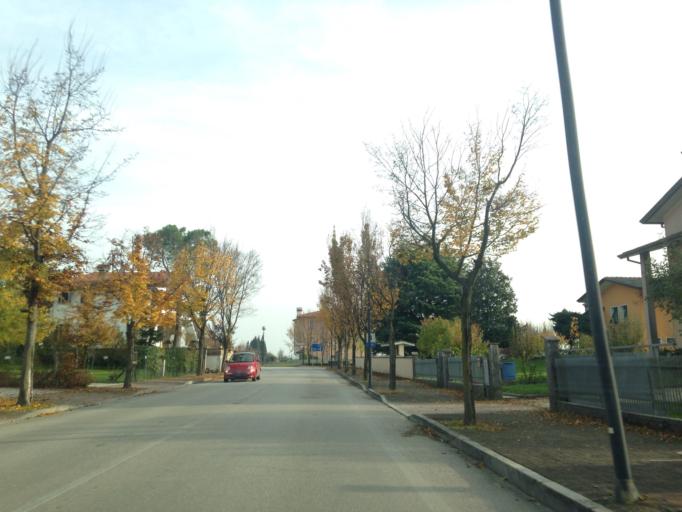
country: IT
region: Veneto
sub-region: Provincia di Treviso
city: Portobuffole
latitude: 45.8773
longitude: 12.5376
